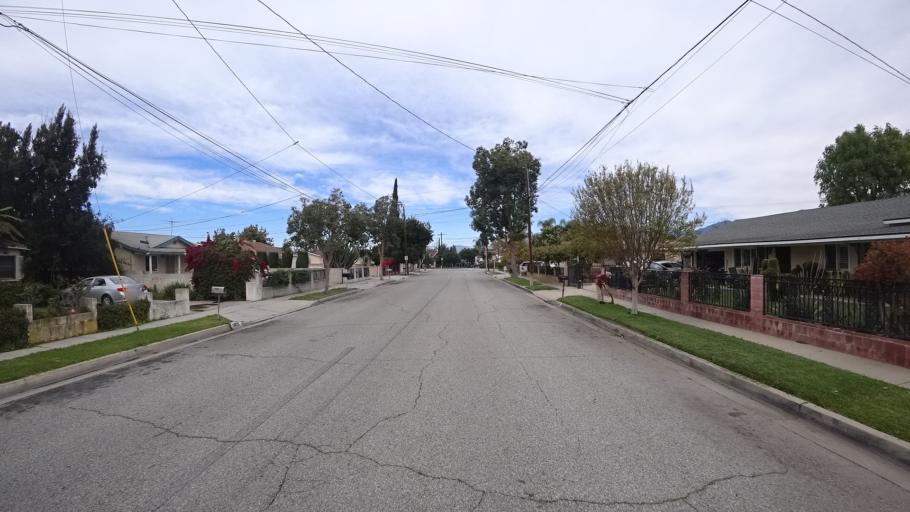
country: US
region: California
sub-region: Los Angeles County
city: Baldwin Park
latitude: 34.0785
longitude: -117.9748
